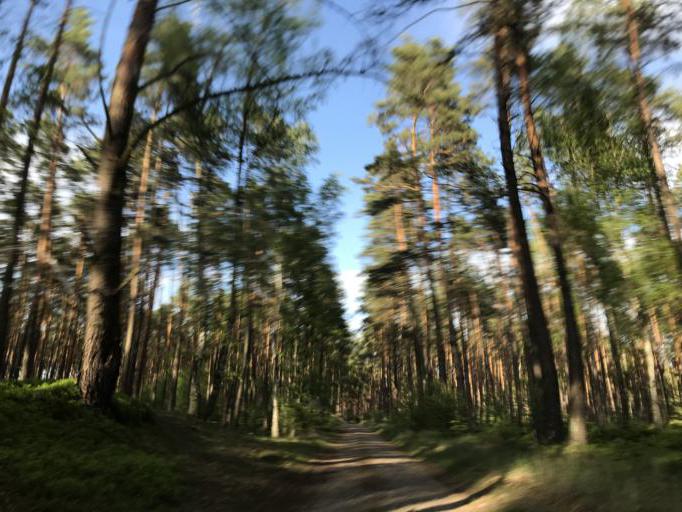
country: DE
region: Brandenburg
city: Joachimsthal
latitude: 52.9597
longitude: 13.6843
